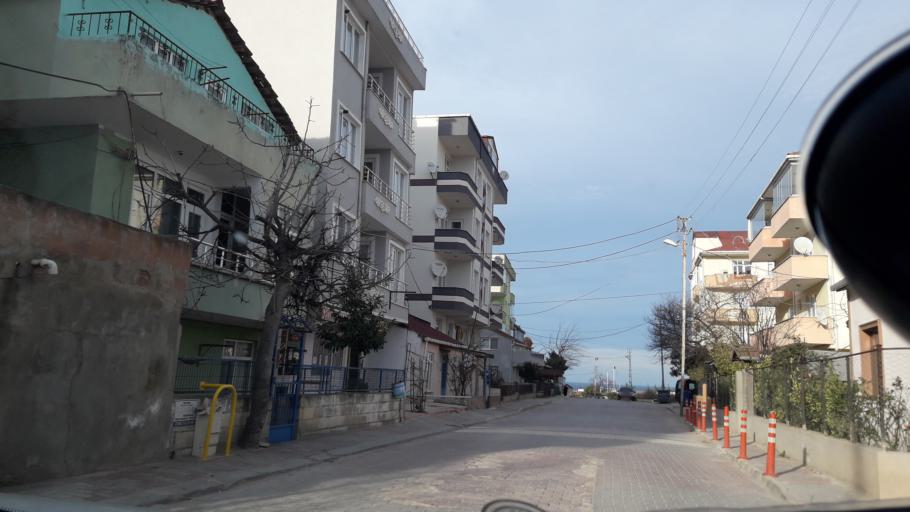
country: TR
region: Sinop
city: Gerze
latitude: 41.8062
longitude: 35.1900
